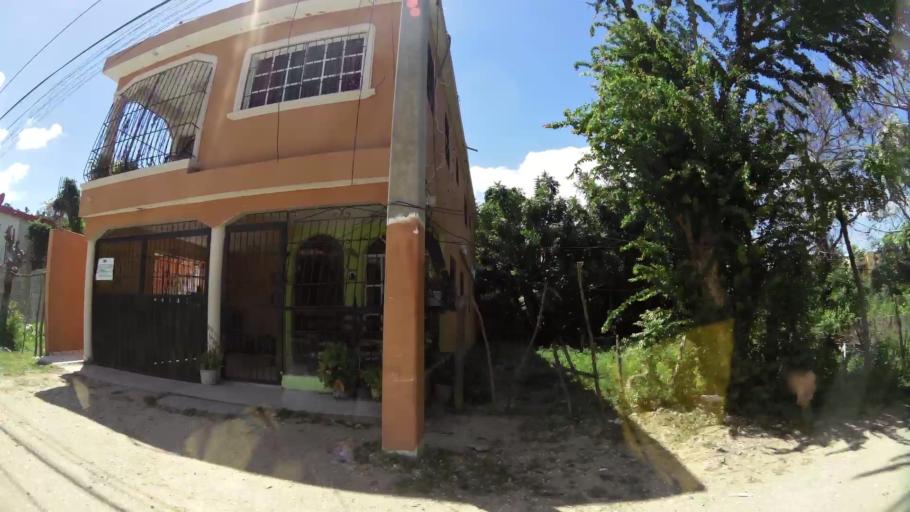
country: DO
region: San Cristobal
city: San Cristobal
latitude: 18.4110
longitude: -70.0924
